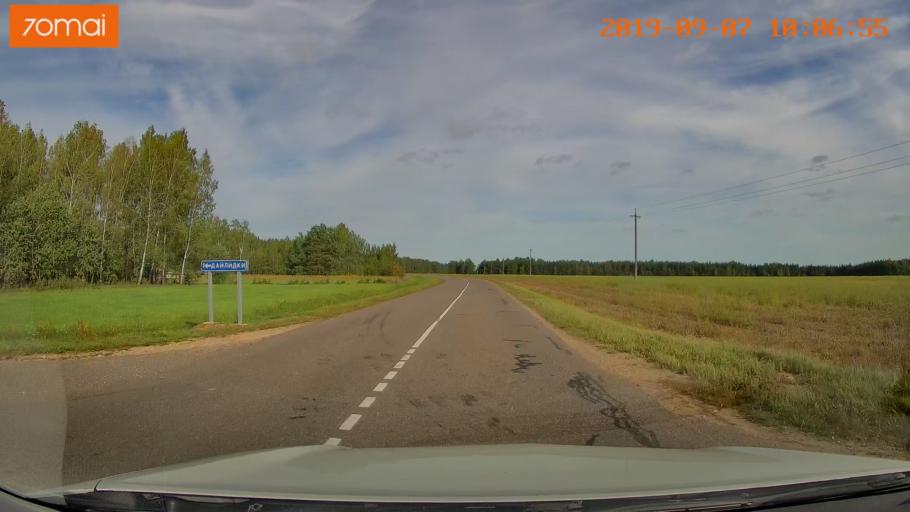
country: BY
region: Grodnenskaya
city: Voranava
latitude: 54.0683
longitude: 25.3989
